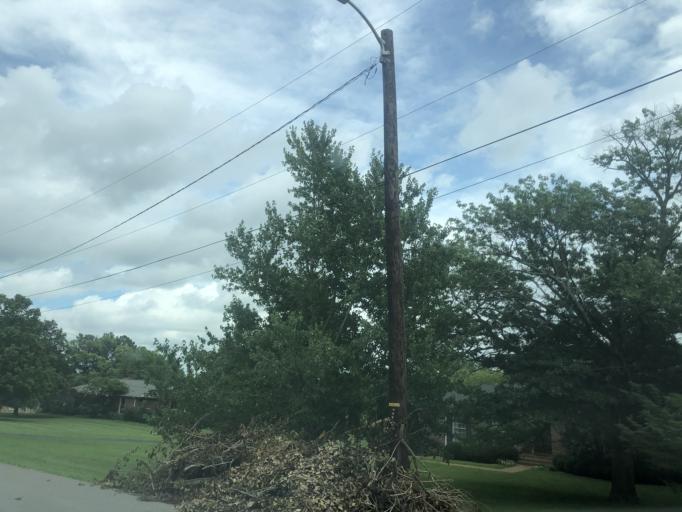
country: US
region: Tennessee
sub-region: Davidson County
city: Oak Hill
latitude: 36.0783
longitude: -86.8082
